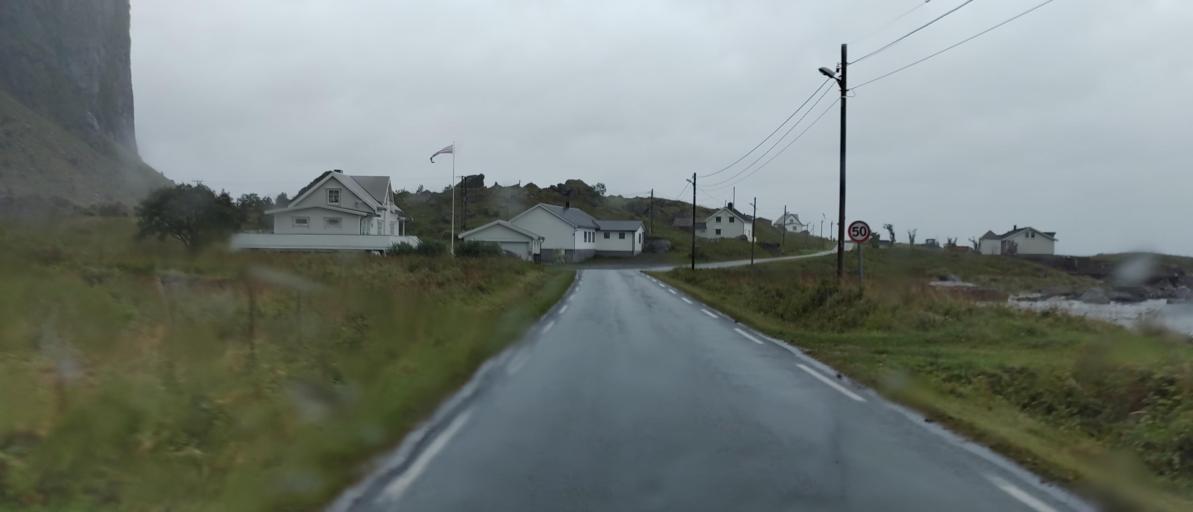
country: NO
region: Nordland
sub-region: Vestvagoy
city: Evjen
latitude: 68.3038
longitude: 13.6987
